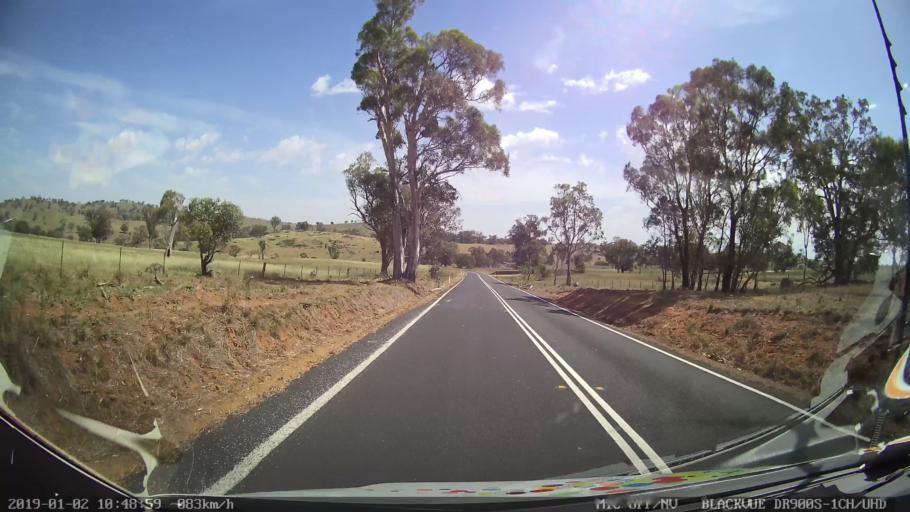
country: AU
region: New South Wales
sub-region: Cootamundra
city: Cootamundra
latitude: -34.7303
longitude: 148.2776
